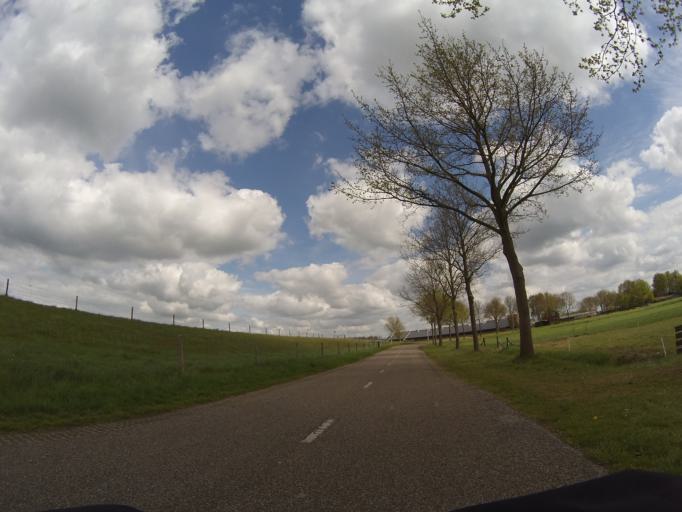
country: NL
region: Overijssel
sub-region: Gemeente Zwolle
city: Zwolle
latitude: 52.5223
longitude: 6.1536
